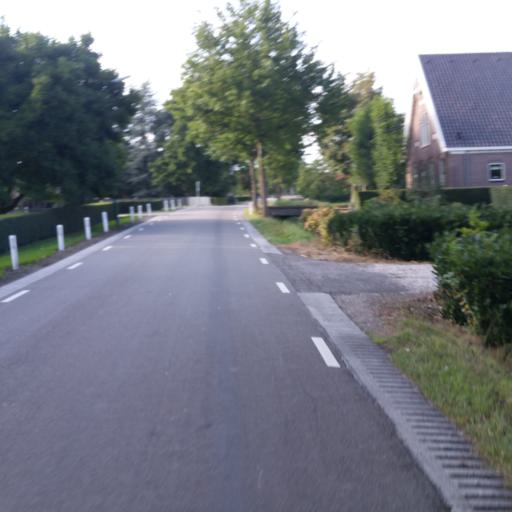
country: NL
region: Utrecht
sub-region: Gemeente IJsselstein
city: IJsselstein
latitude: 52.0301
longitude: 5.0270
